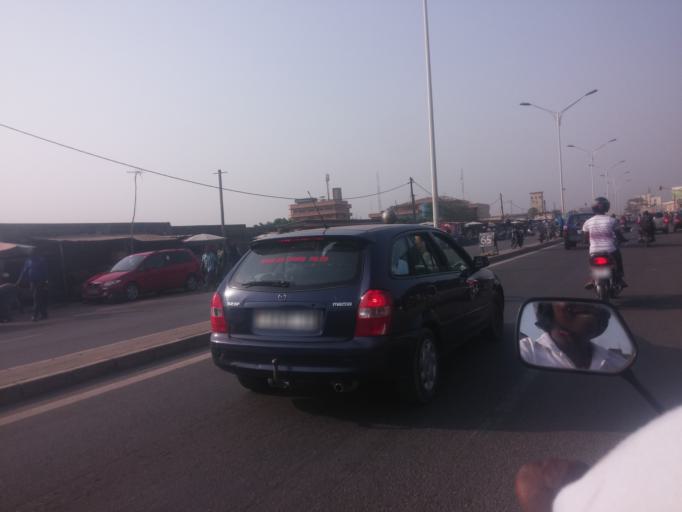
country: TG
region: Maritime
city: Lome
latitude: 6.1571
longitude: 1.2854
